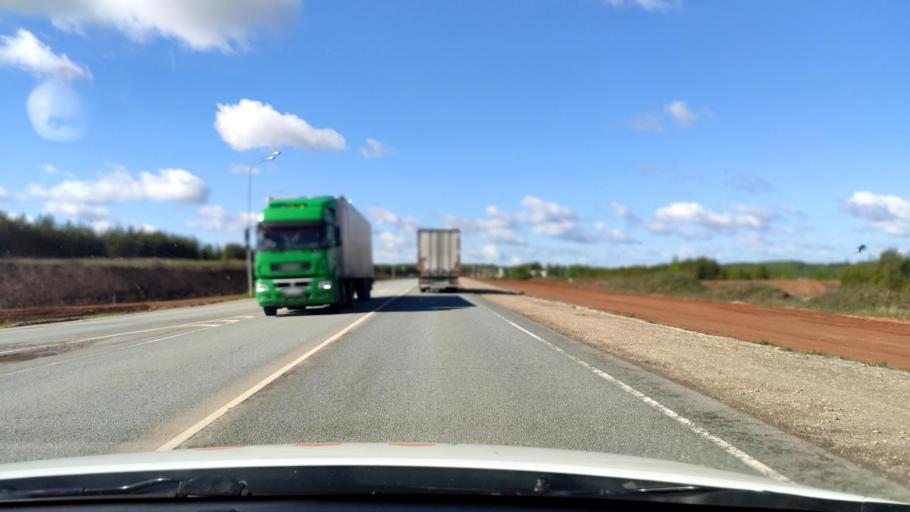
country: RU
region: Tatarstan
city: Sviyazhsk
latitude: 55.7364
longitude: 48.7817
